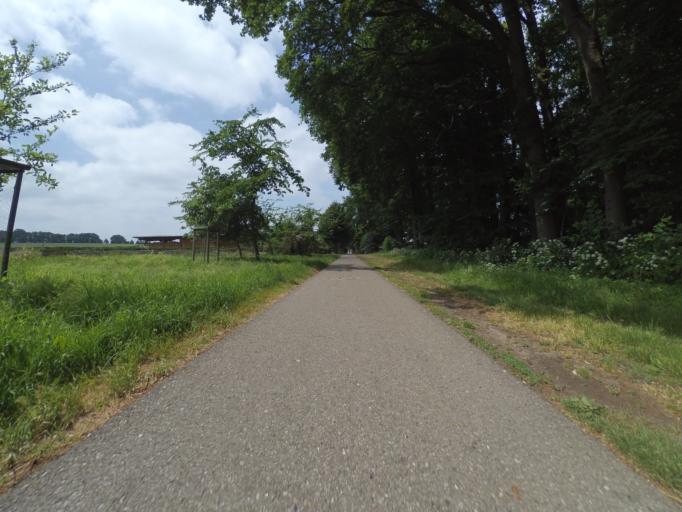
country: DE
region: Mecklenburg-Vorpommern
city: Malchow
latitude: 53.4907
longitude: 12.4977
